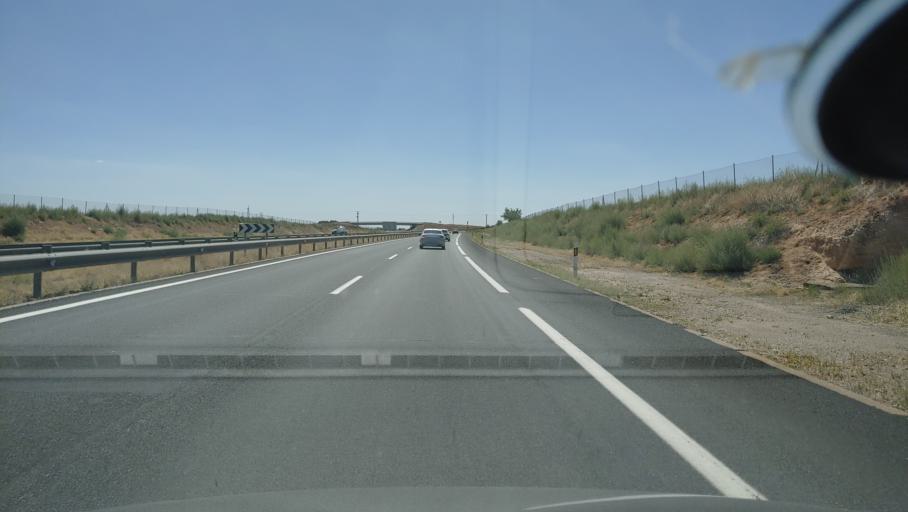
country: ES
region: Castille-La Mancha
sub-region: Provincia de Ciudad Real
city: Villarta de San Juan
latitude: 39.2268
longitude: -3.4114
